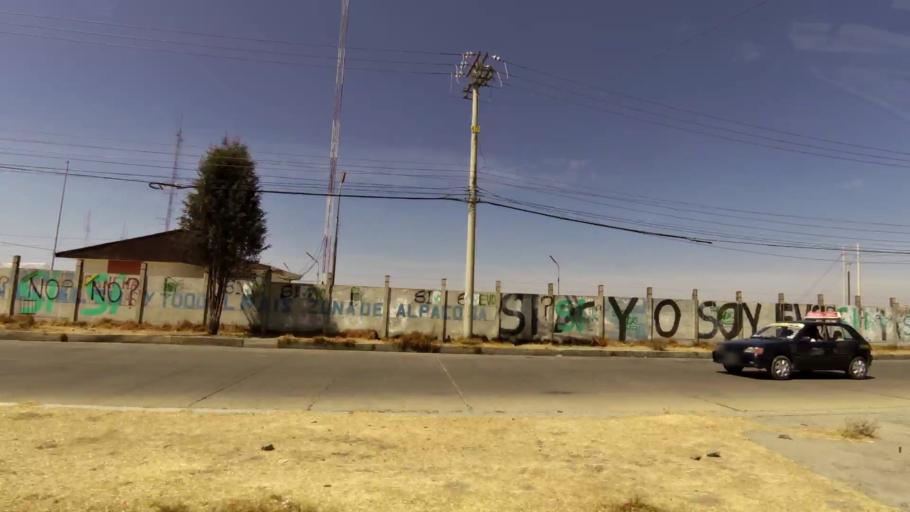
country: BO
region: La Paz
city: La Paz
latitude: -16.5288
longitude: -68.1454
